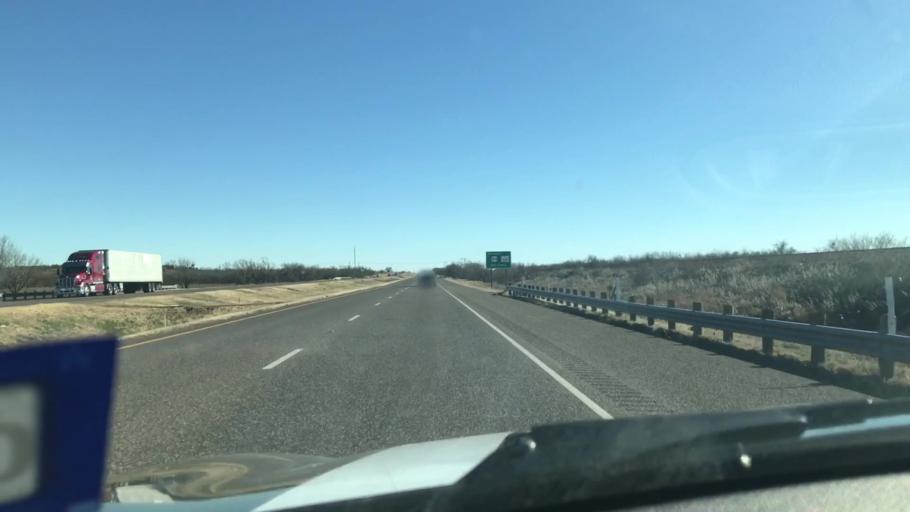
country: US
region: Texas
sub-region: Scurry County
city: Snyder
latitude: 32.8123
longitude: -100.9740
